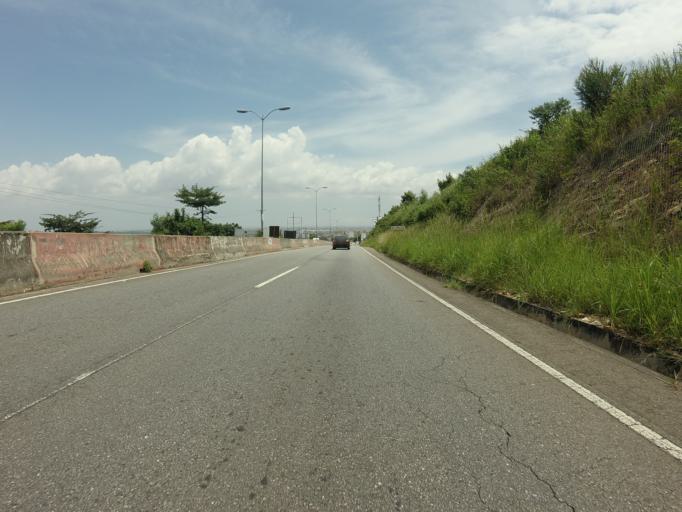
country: GH
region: Eastern
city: Aburi
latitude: 5.7879
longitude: -0.1840
